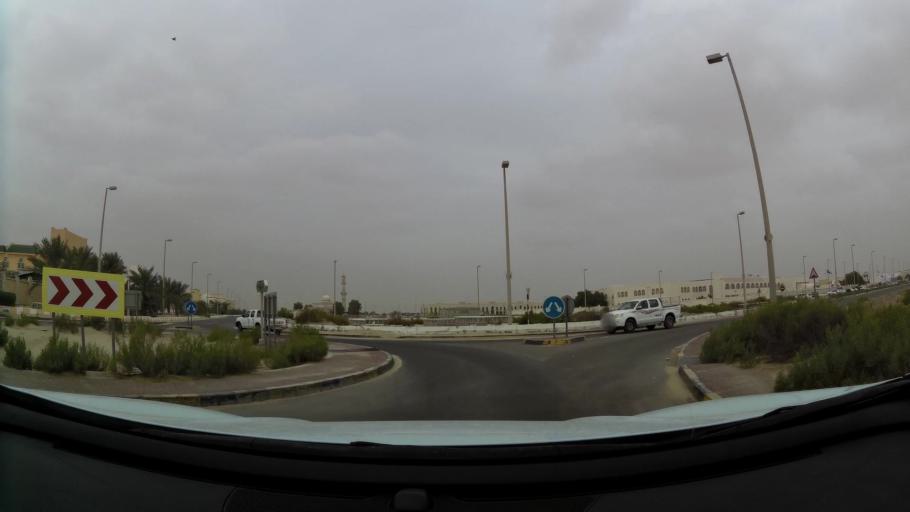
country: AE
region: Abu Dhabi
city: Abu Dhabi
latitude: 24.3721
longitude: 54.6631
